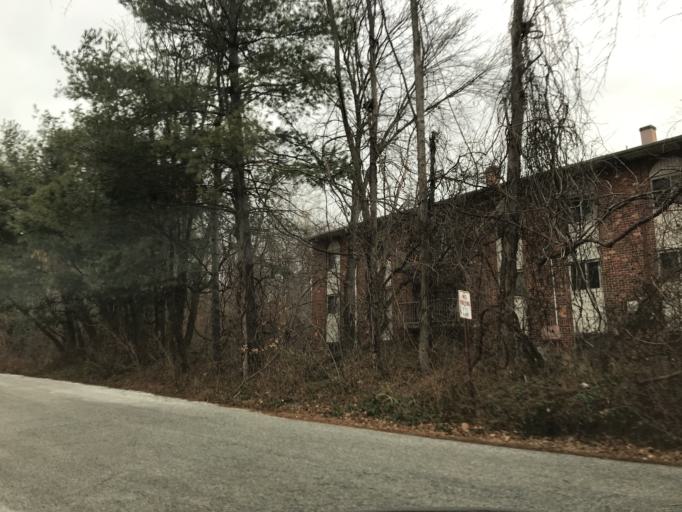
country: US
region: Maryland
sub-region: Baltimore County
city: Middle River
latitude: 39.3361
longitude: -76.4504
